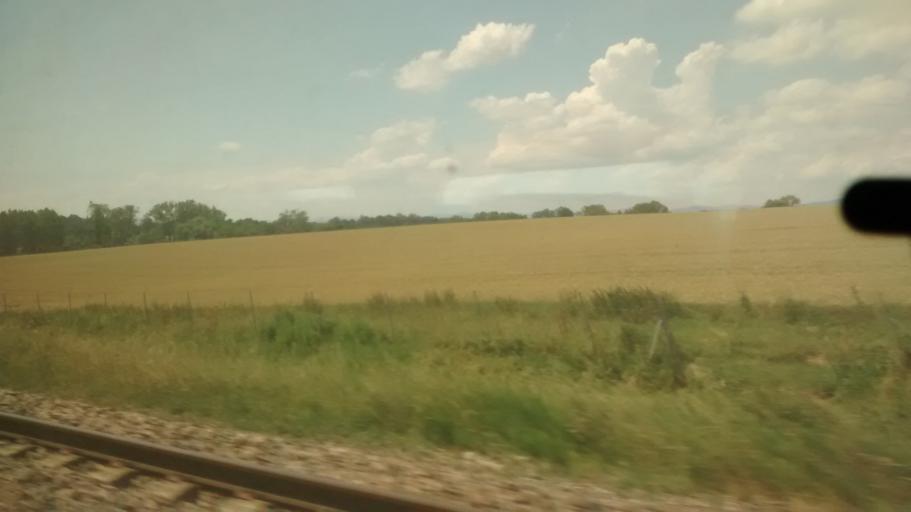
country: FR
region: Rhone-Alpes
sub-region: Departement de l'Ain
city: Grieges
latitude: 46.2104
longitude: 4.8573
